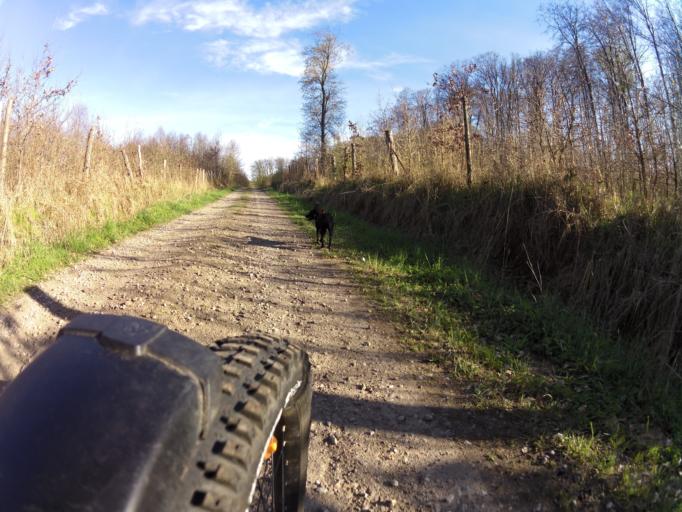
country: PL
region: West Pomeranian Voivodeship
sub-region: Powiat lobeski
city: Lobez
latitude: 53.7600
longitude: 15.5898
